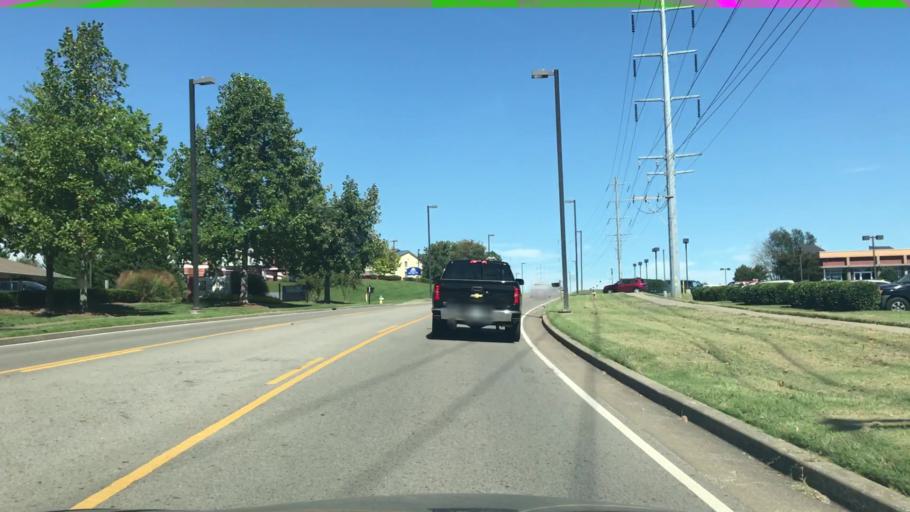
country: US
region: Tennessee
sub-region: Williamson County
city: Franklin
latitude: 35.9088
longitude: -86.8238
